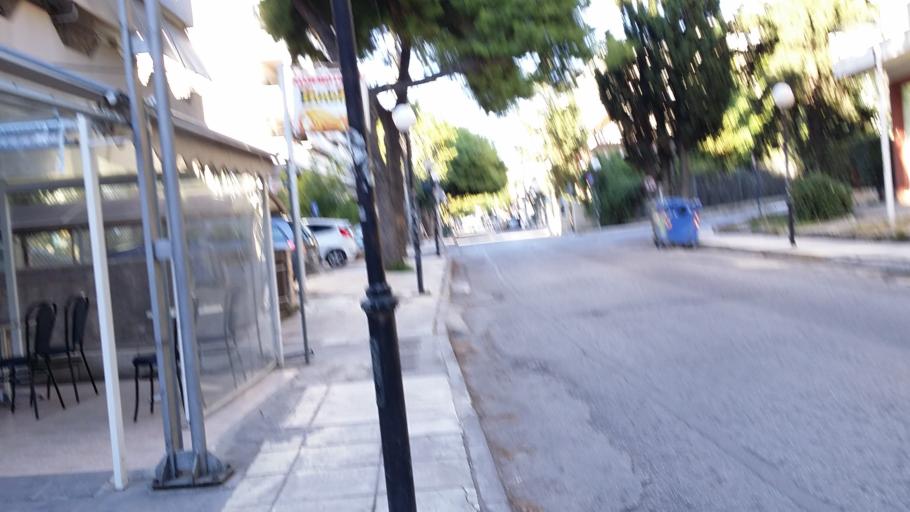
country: GR
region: Attica
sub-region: Nomarchia Athinas
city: Irakleio
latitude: 38.0564
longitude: 23.7569
